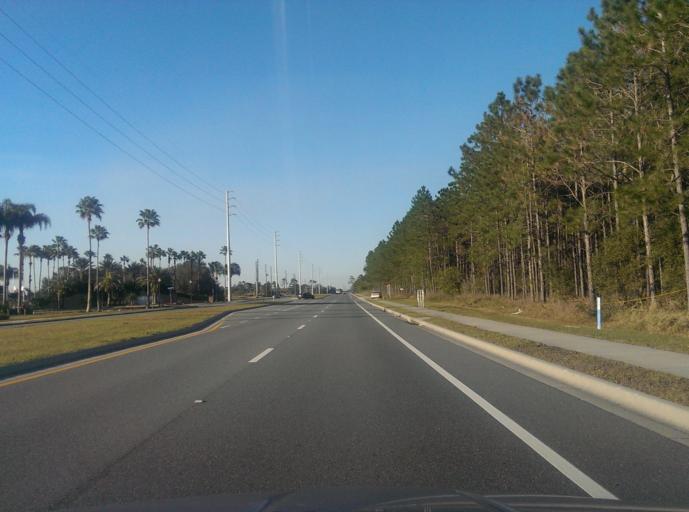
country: US
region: Florida
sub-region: Polk County
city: Citrus Ridge
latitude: 28.3151
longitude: -81.5906
